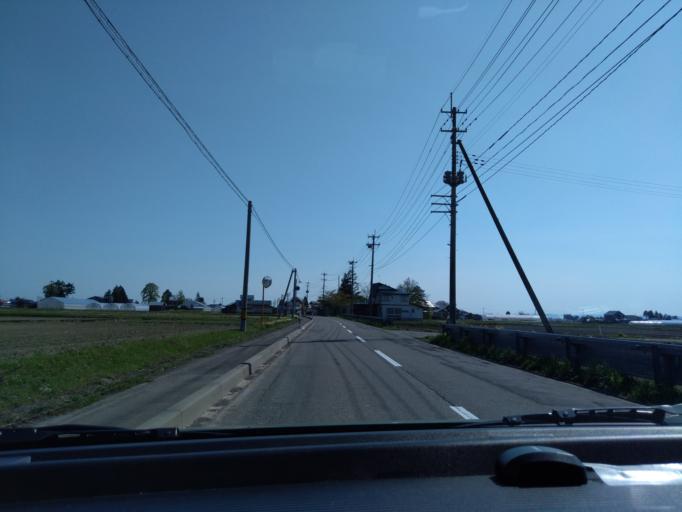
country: JP
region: Akita
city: Omagari
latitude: 39.4470
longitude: 140.5676
